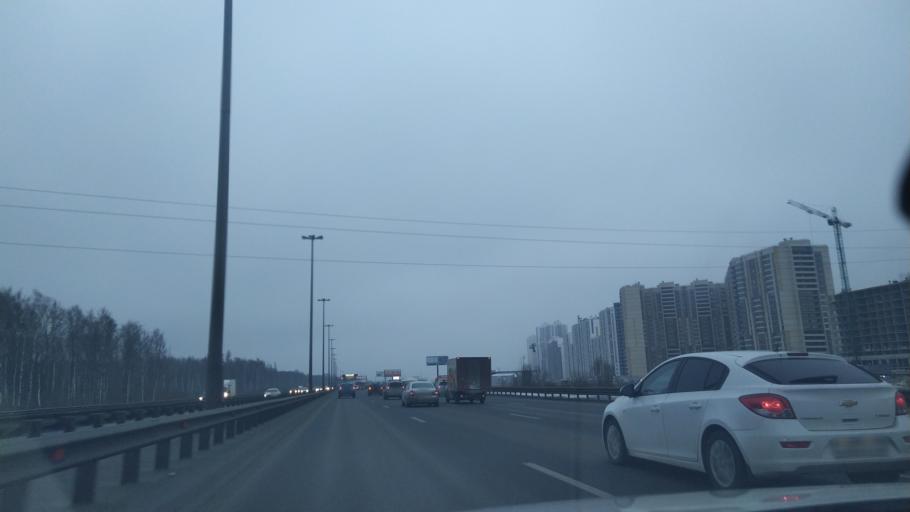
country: RU
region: Leningrad
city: Rybatskoye
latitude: 59.9108
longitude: 30.5259
